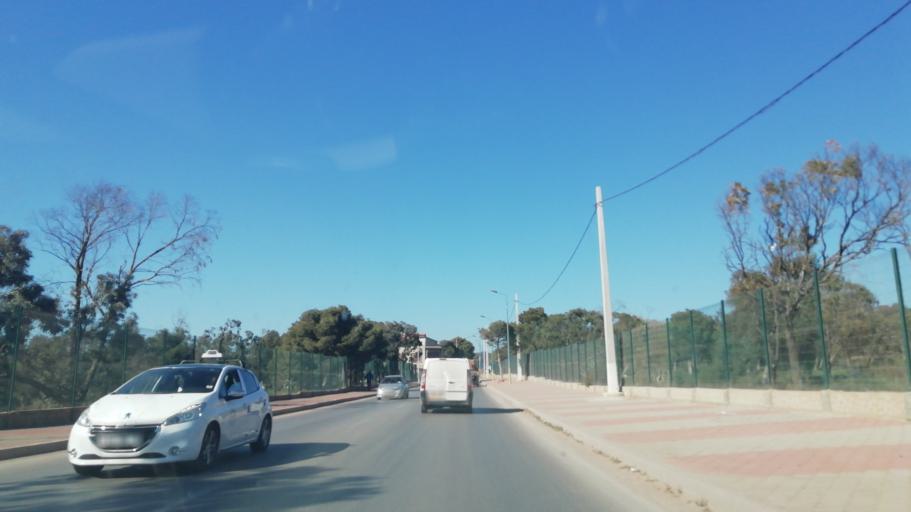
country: DZ
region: Oran
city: Bir el Djir
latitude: 35.7429
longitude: -0.5681
